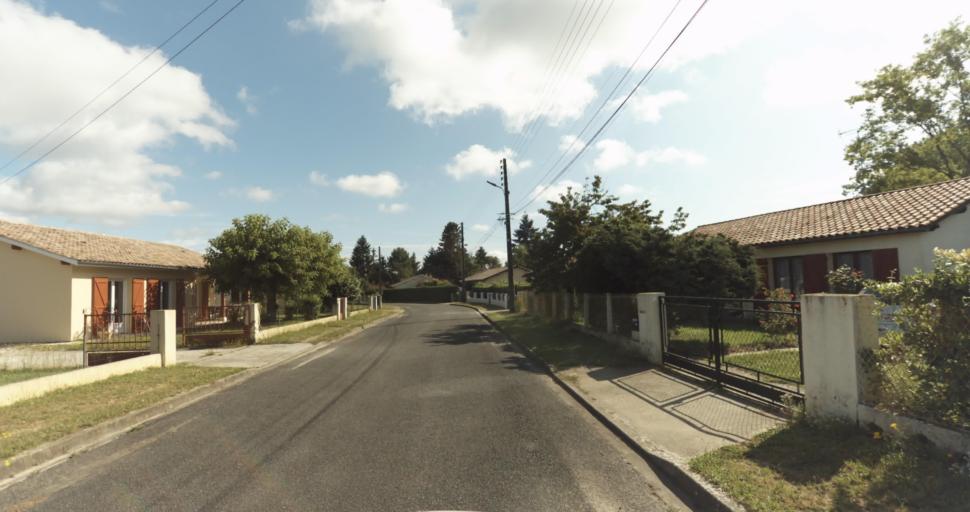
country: FR
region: Aquitaine
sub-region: Departement de la Gironde
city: Bazas
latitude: 44.4276
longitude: -0.2094
